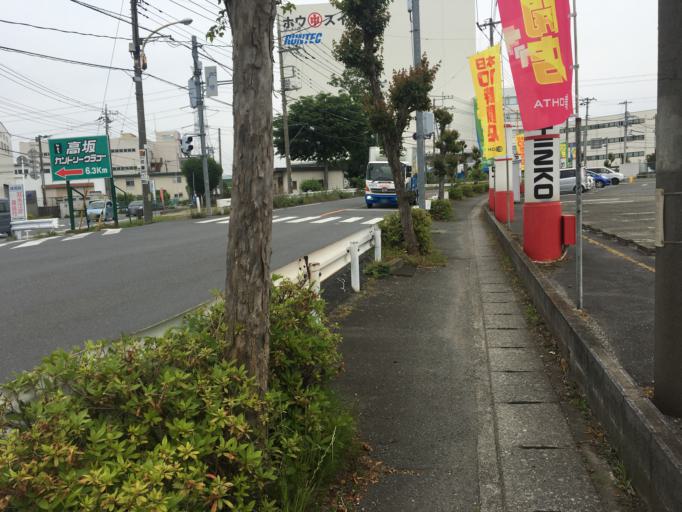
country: JP
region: Saitama
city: Sakado
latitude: 35.9943
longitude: 139.4387
